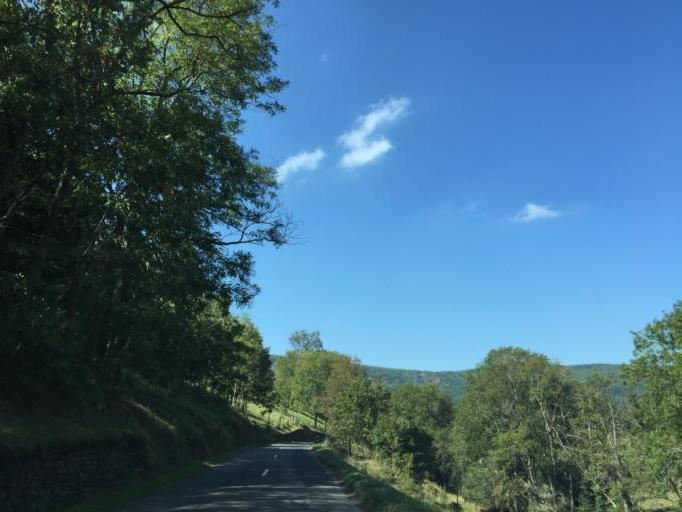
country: FR
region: Rhone-Alpes
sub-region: Departement de la Loire
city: Saint-Paul-en-Jarez
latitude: 45.4292
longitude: 4.5806
